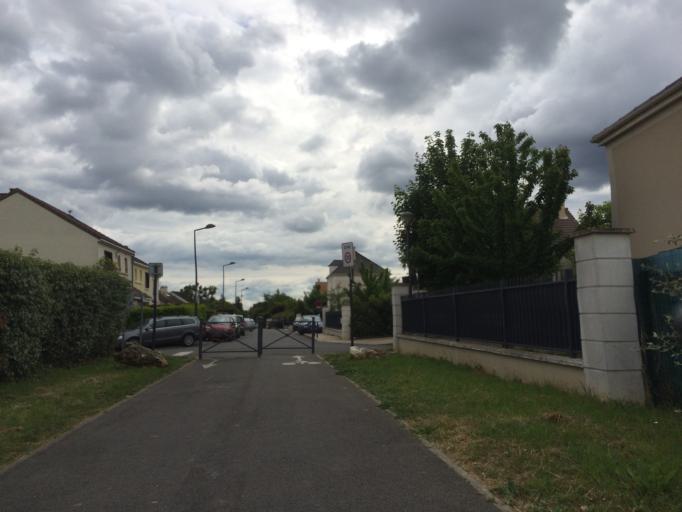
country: FR
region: Ile-de-France
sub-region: Departement de l'Essonne
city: Villiers-sur-Orge
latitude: 48.6623
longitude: 2.2995
